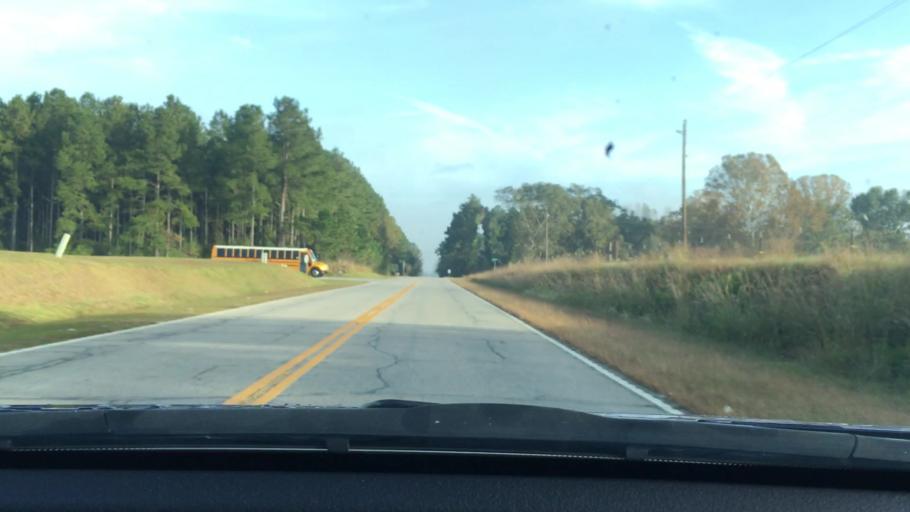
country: US
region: South Carolina
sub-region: Sumter County
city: East Sumter
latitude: 33.9725
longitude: -80.2997
